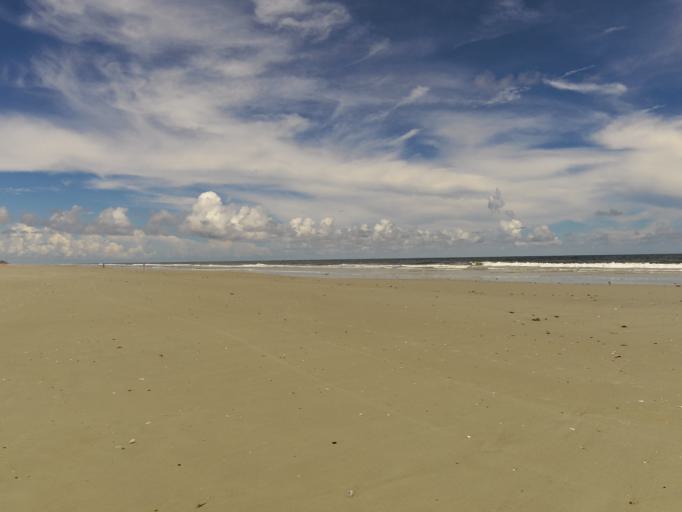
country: US
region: Florida
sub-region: Duval County
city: Atlantic Beach
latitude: 30.4650
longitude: -81.4112
